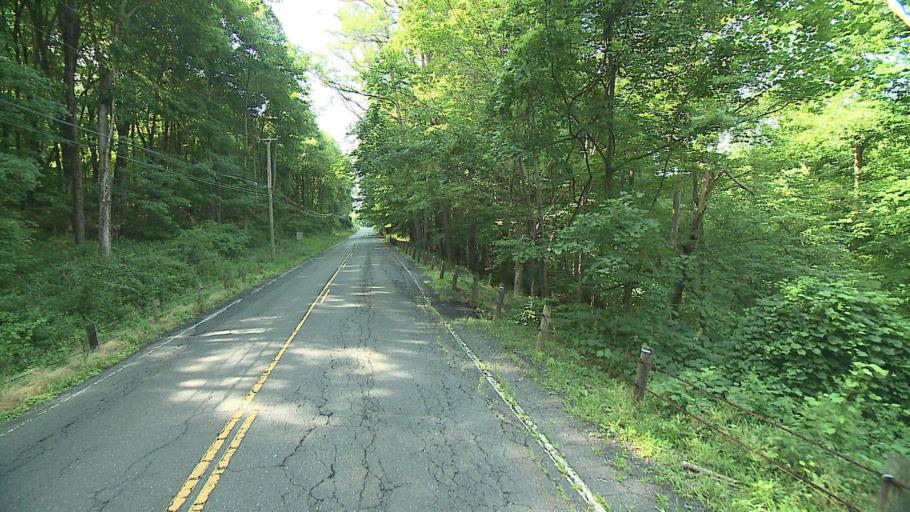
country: US
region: New York
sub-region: Putnam County
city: Putnam Lake
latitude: 41.5043
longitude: -73.5289
